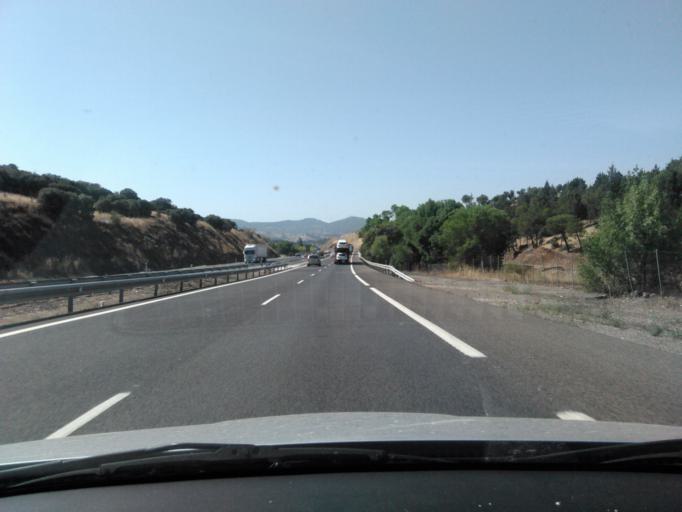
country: ES
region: Castille-La Mancha
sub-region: Provincia de Ciudad Real
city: Viso del Marques
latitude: 38.4514
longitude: -3.4970
